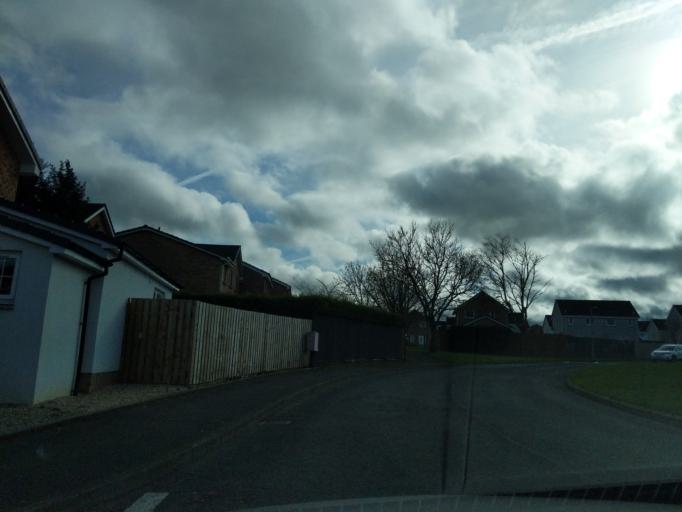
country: GB
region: Scotland
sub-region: Edinburgh
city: Queensferry
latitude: 55.9861
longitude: -3.4095
